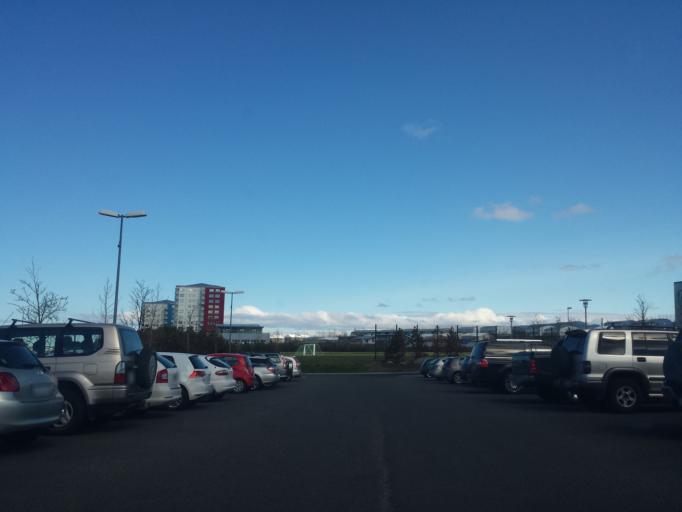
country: IS
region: Capital Region
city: Reykjavik
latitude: 64.0916
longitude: -21.8569
